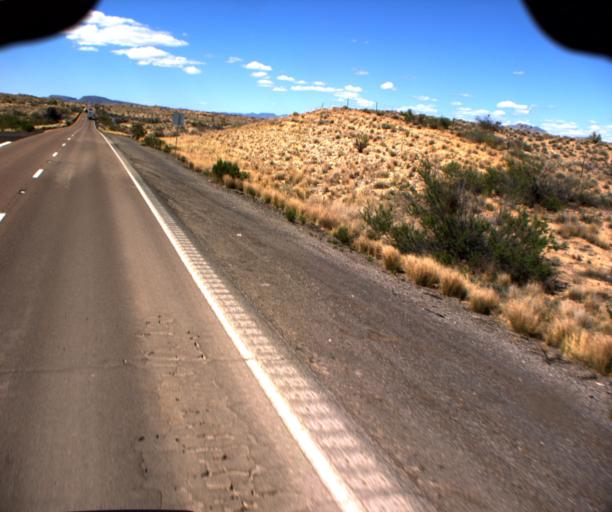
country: US
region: Arizona
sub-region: Mohave County
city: Kingman
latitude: 35.0564
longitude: -113.6648
